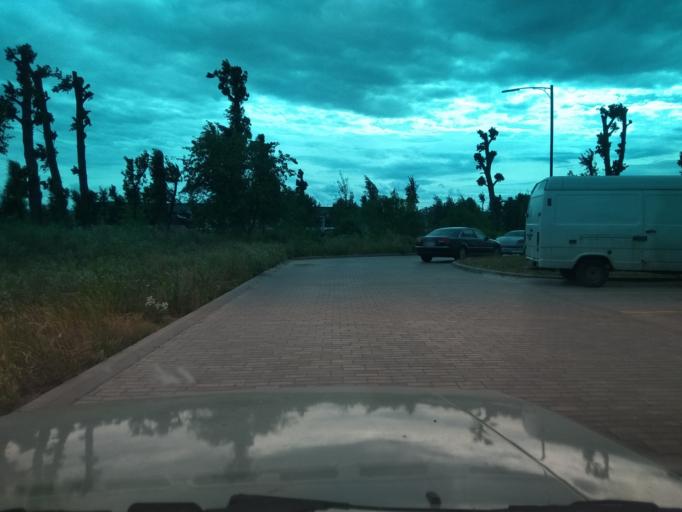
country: BY
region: Mogilev
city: Mahilyow
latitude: 53.9219
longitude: 30.3546
